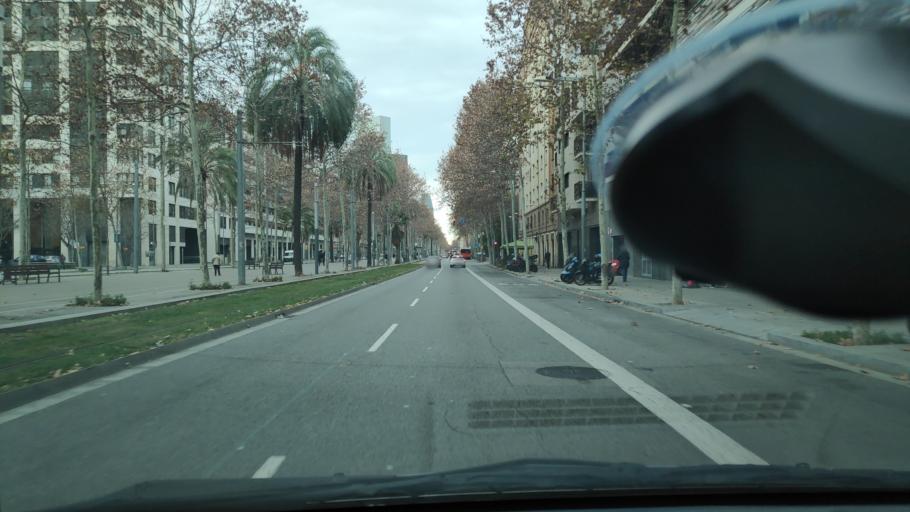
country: ES
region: Catalonia
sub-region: Provincia de Barcelona
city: Sant Marti
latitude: 41.4084
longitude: 2.2067
